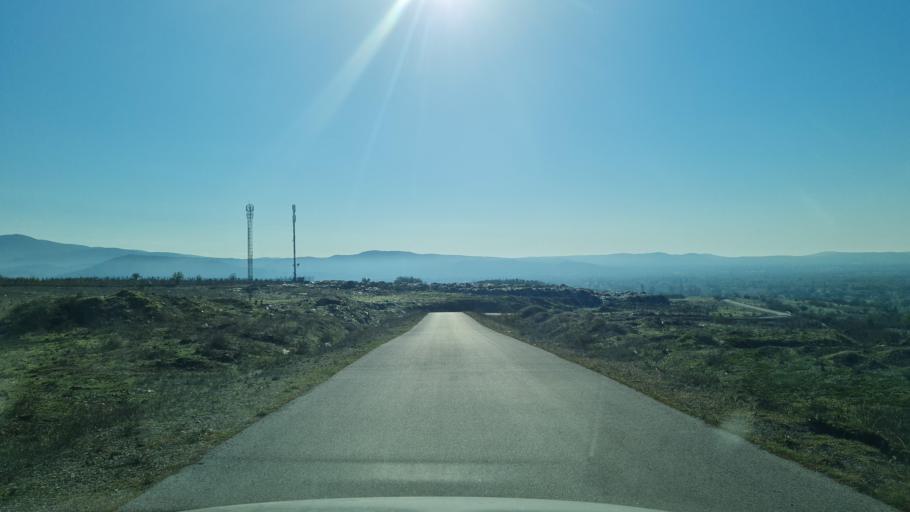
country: MK
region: Bogdanci
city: Bogdanci
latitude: 41.2009
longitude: 22.5604
